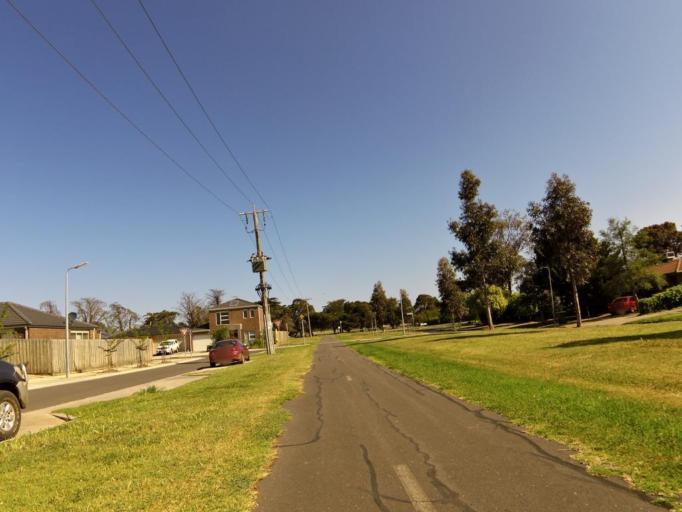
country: AU
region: Victoria
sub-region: Wyndham
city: Werribee
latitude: -37.9112
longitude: 144.6772
